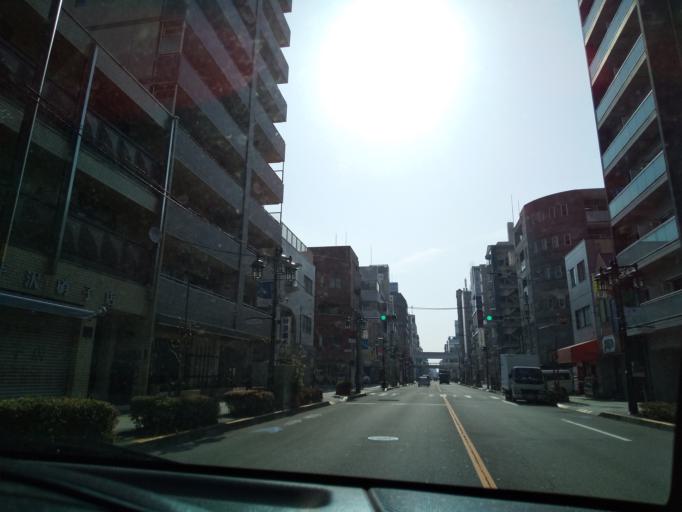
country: JP
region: Tokyo
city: Hino
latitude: 35.6965
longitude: 139.4098
